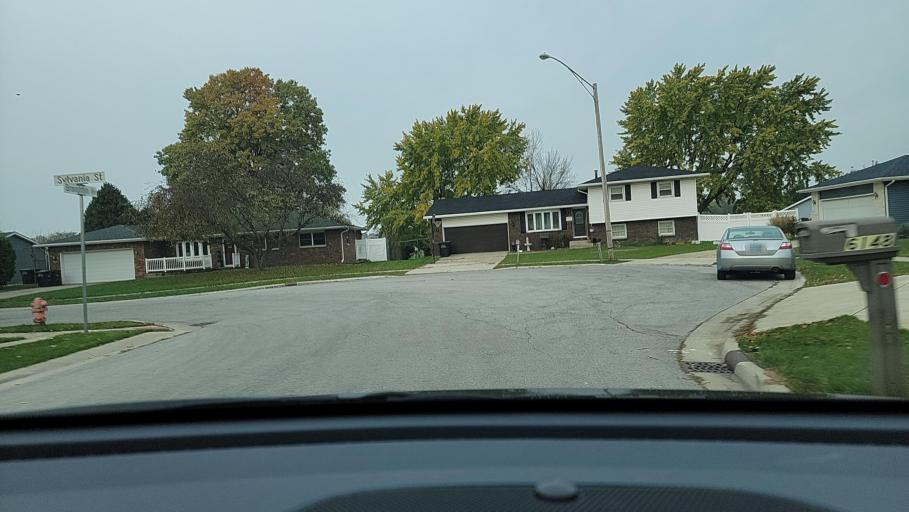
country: US
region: Indiana
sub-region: Porter County
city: Portage
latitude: 41.5611
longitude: -87.1772
